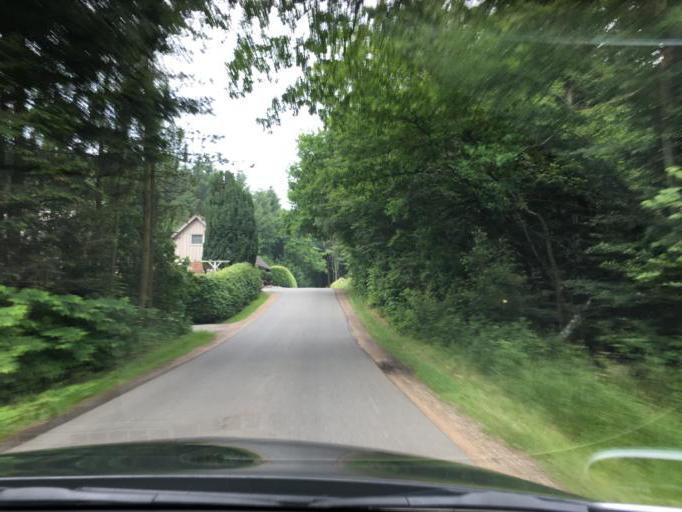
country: DK
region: South Denmark
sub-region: Vejle Kommune
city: Vejle
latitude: 55.6163
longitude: 9.5015
